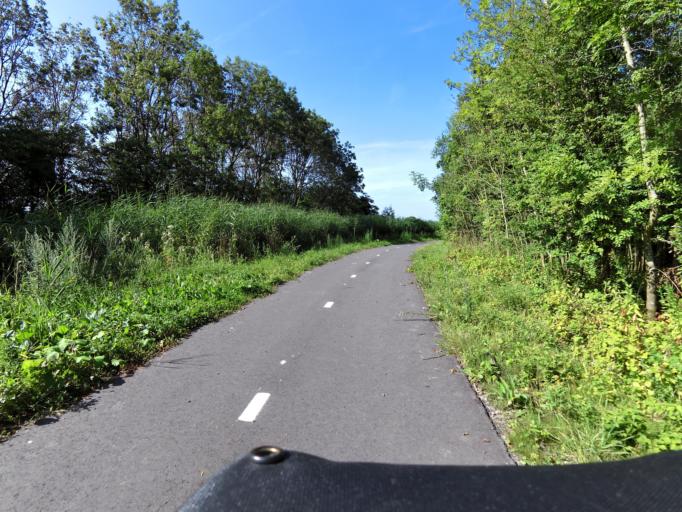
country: NL
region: South Holland
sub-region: Gemeente Goeree-Overflakkee
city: Dirksland
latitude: 51.7364
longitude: 4.0823
